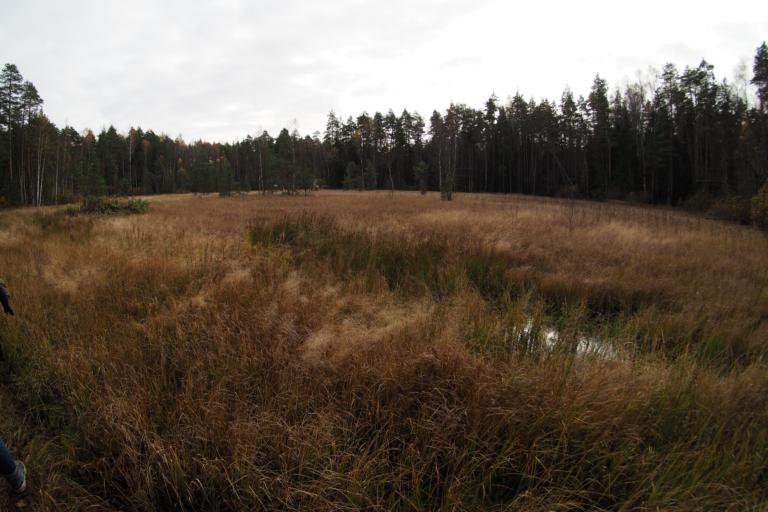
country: RU
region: Moskovskaya
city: Davydovo
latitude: 55.5605
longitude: 38.7817
